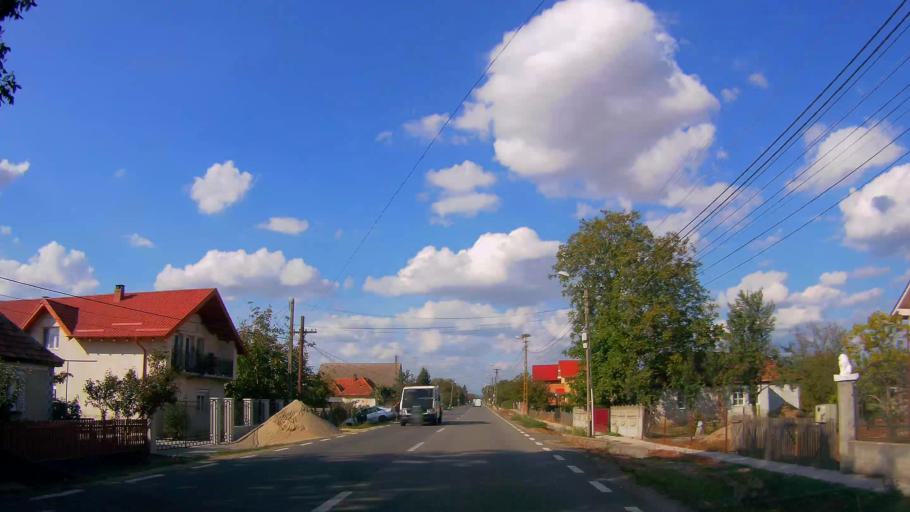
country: RO
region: Satu Mare
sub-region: Comuna Turulung
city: Draguseni
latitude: 47.8981
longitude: 23.0748
